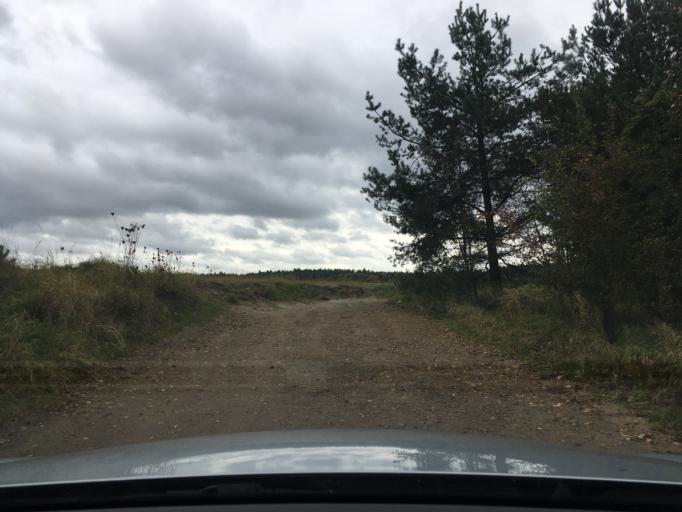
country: PL
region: Pomeranian Voivodeship
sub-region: Powiat koscierski
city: Koscierzyna
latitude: 54.1133
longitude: 18.0037
